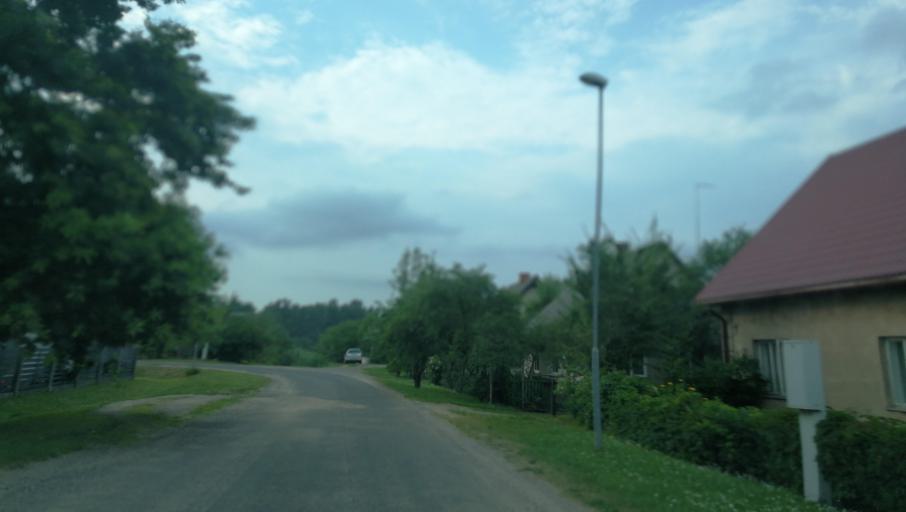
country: LV
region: Cesu Rajons
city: Cesis
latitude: 57.3203
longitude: 25.2728
